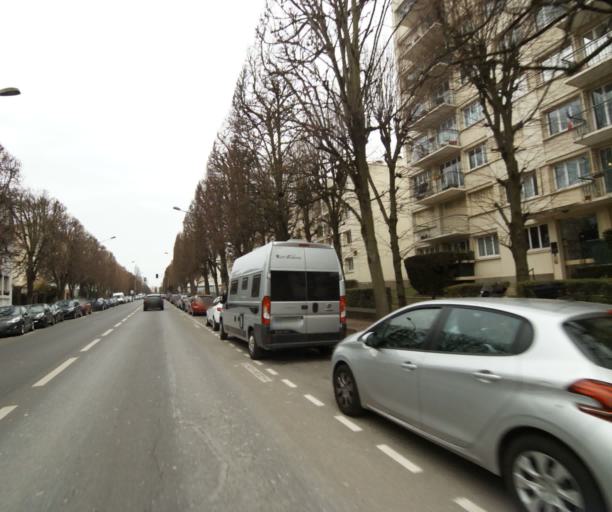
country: FR
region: Ile-de-France
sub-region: Departement des Hauts-de-Seine
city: Saint-Cloud
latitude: 48.8554
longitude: 2.2117
